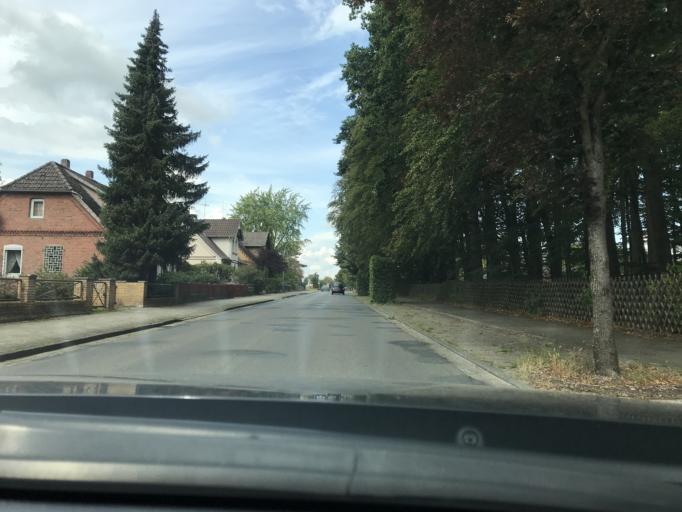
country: DE
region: Lower Saxony
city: Suderburg
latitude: 52.8954
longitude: 10.4437
